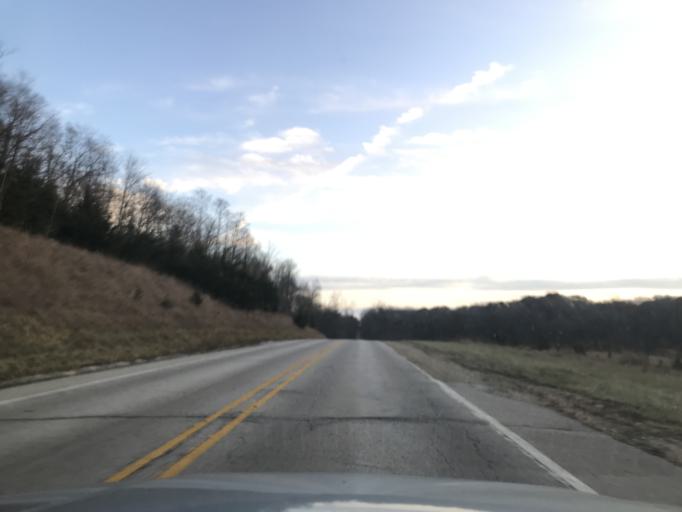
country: US
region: Illinois
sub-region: Henderson County
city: Oquawka
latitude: 40.9064
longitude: -90.8644
